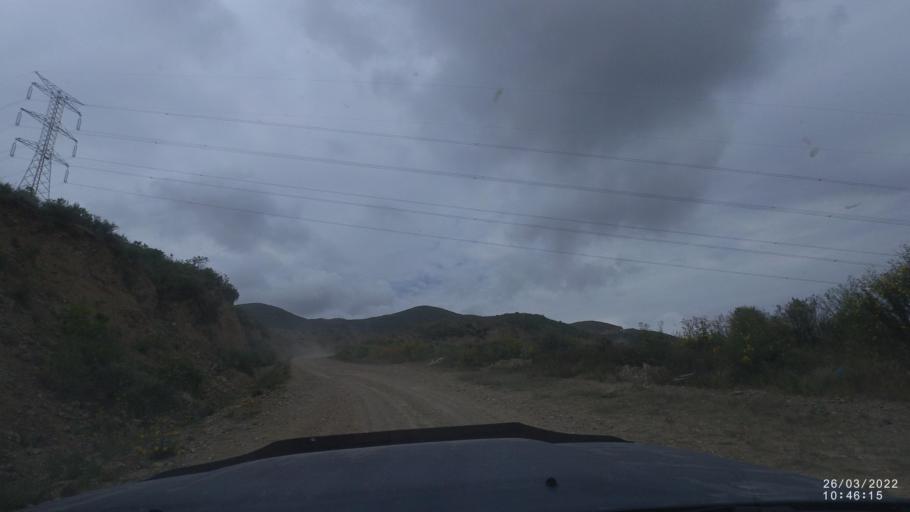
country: BO
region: Cochabamba
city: Tarata
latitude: -17.4856
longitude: -66.0490
